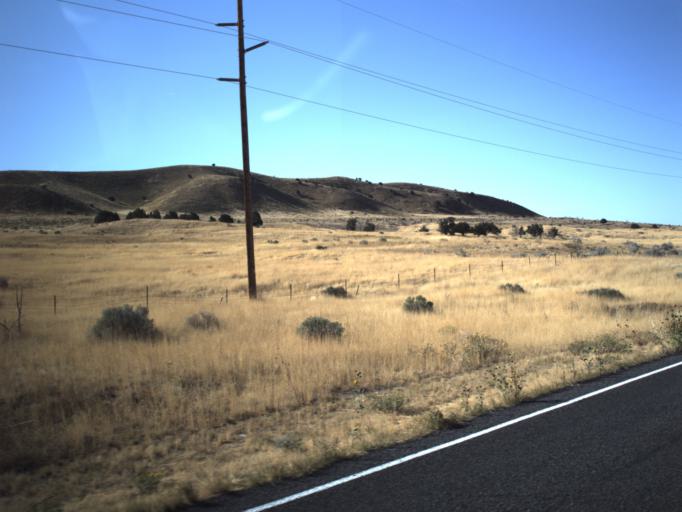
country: US
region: Utah
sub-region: Millard County
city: Delta
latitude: 39.4443
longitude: -112.3124
